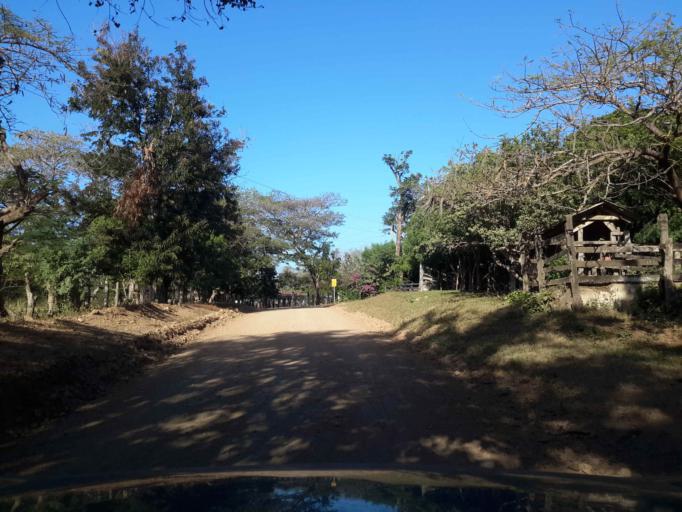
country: NI
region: Rivas
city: San Juan del Sur
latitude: 11.1979
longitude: -85.8053
